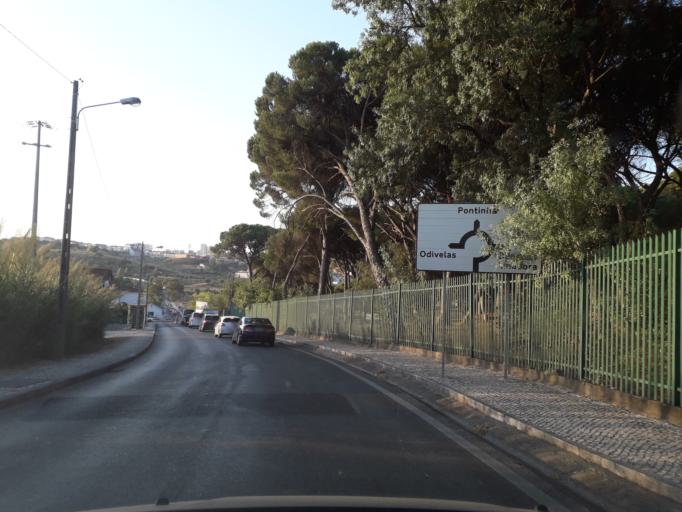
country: PT
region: Lisbon
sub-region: Odivelas
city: Famoes
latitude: 38.7773
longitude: -9.2060
